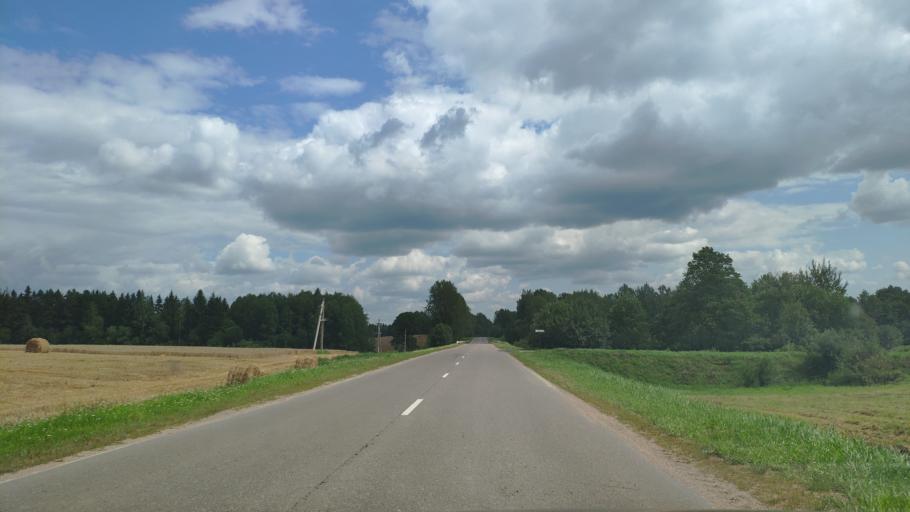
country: BY
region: Minsk
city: Khatsyezhyna
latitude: 53.8803
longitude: 27.2811
